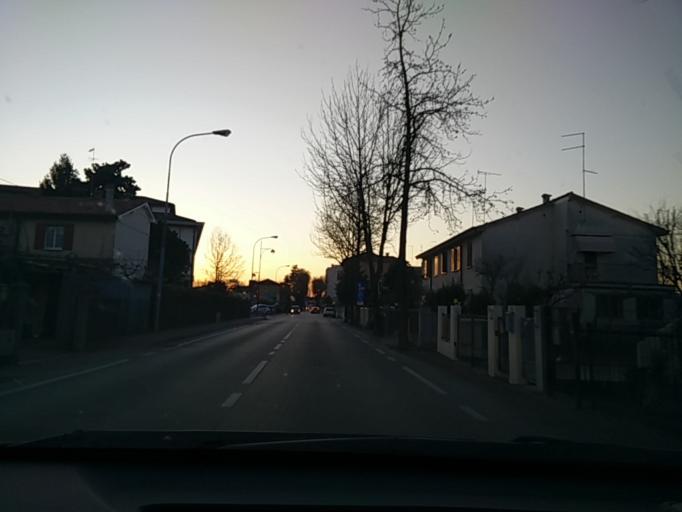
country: IT
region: Veneto
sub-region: Provincia di Venezia
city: San Dona di Piave
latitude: 45.6355
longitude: 12.5672
